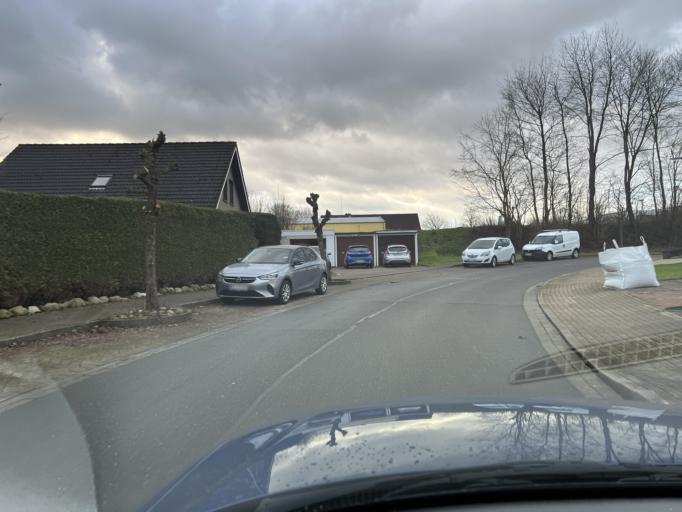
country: DE
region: Schleswig-Holstein
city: Ostrohe
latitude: 54.2000
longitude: 9.1275
